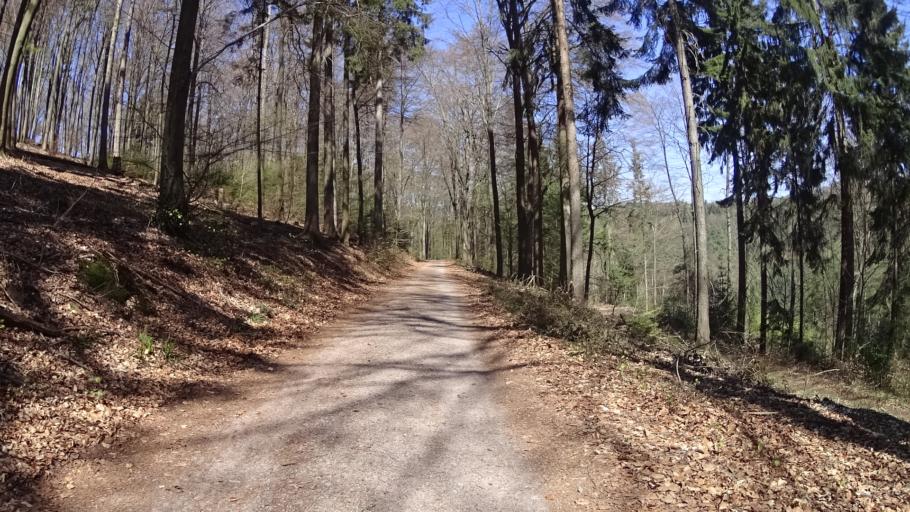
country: DE
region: Rheinland-Pfalz
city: Neidenfels
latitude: 49.4080
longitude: 8.0711
